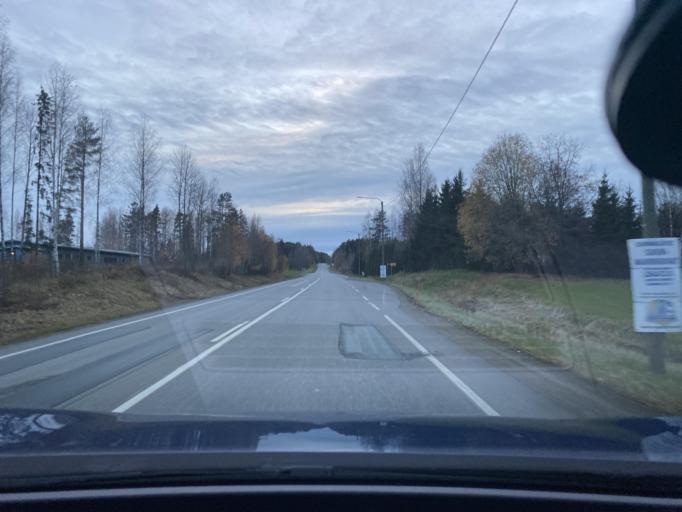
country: FI
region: Uusimaa
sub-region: Helsinki
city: Saukkola
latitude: 60.3846
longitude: 23.9915
